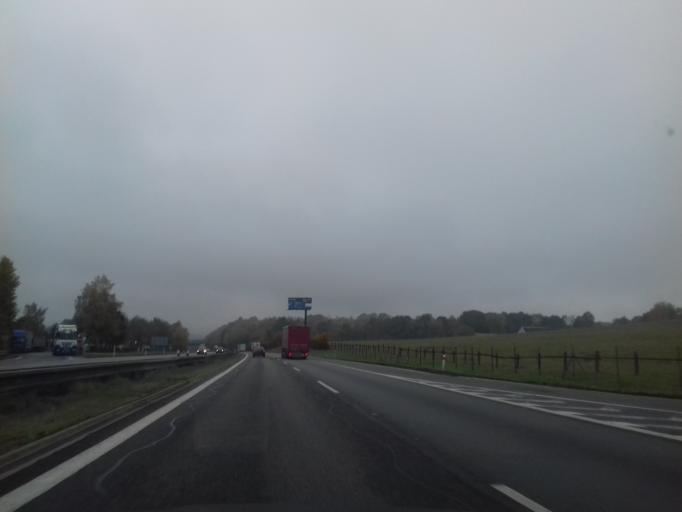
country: CZ
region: Vysocina
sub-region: Okres Pelhrimov
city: Zeliv
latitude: 49.5666
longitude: 15.2868
